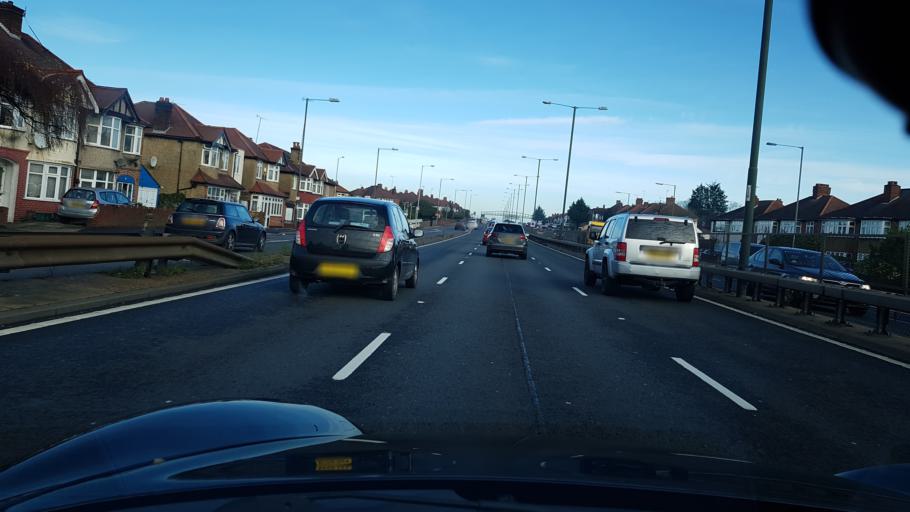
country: GB
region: England
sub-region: Greater London
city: Surbiton
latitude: 51.3818
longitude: -0.2780
